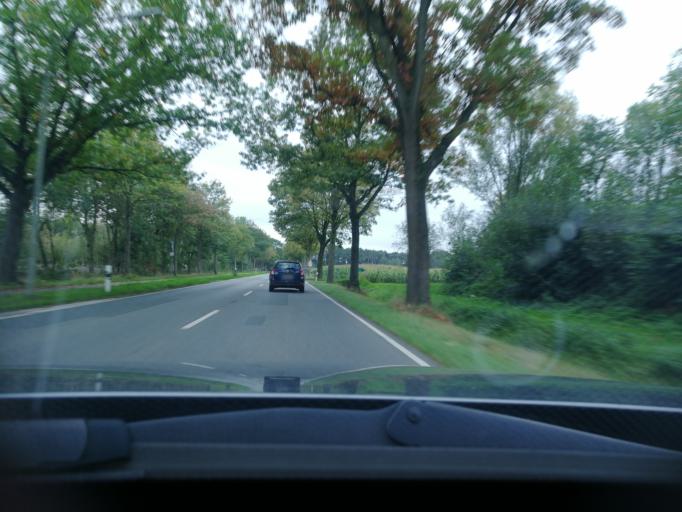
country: DE
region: North Rhine-Westphalia
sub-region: Regierungsbezirk Dusseldorf
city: Kevelaer
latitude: 51.5278
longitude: 6.2424
